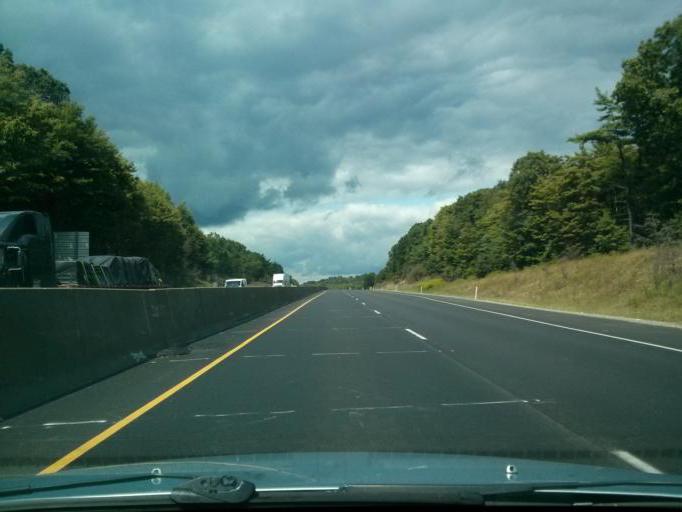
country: US
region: Pennsylvania
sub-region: Clarion County
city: Clarion
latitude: 41.1904
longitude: -79.4198
